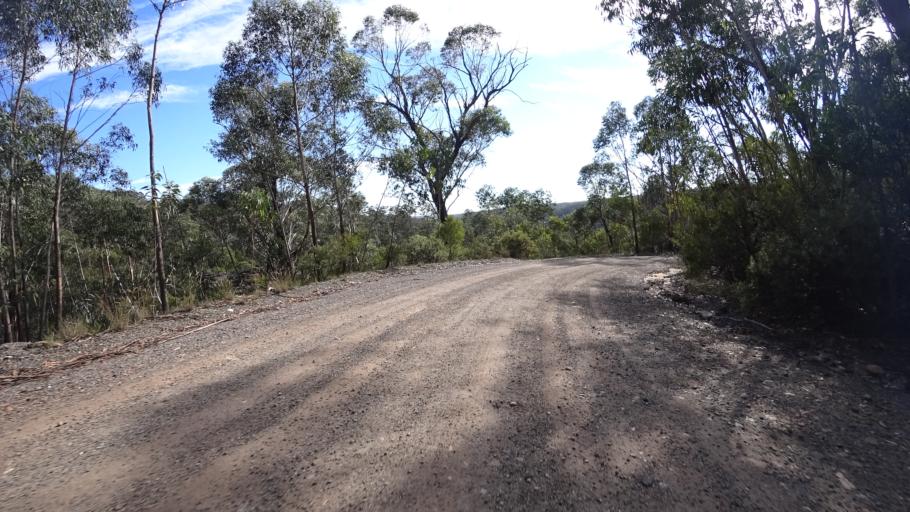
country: AU
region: New South Wales
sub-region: Lithgow
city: Lithgow
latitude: -33.5019
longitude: 150.1666
